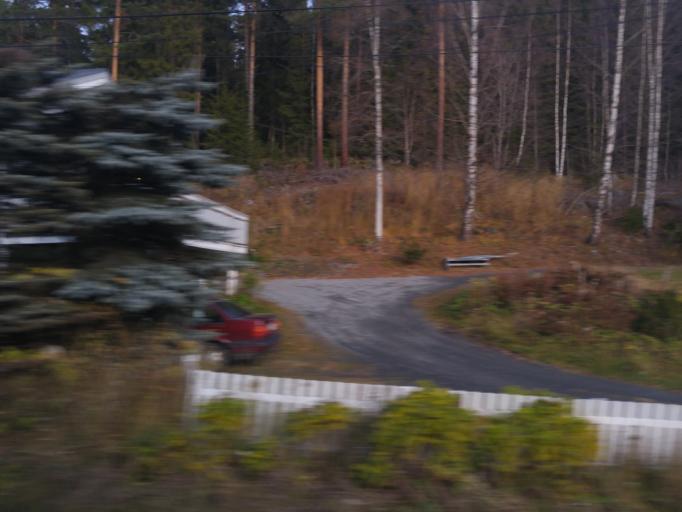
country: NO
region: Oppland
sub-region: Nord-Aurdal
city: Fagernes
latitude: 61.0371
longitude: 9.1759
